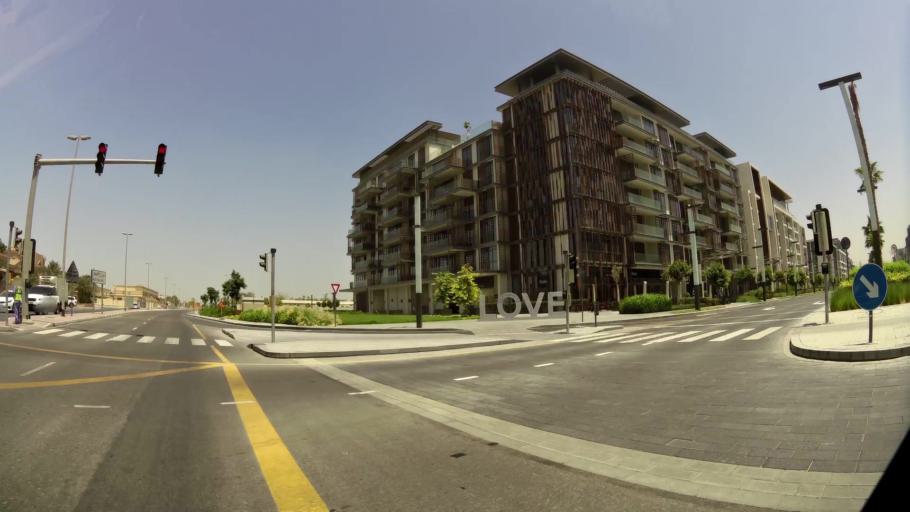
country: AE
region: Dubai
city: Dubai
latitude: 25.2014
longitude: 55.2609
